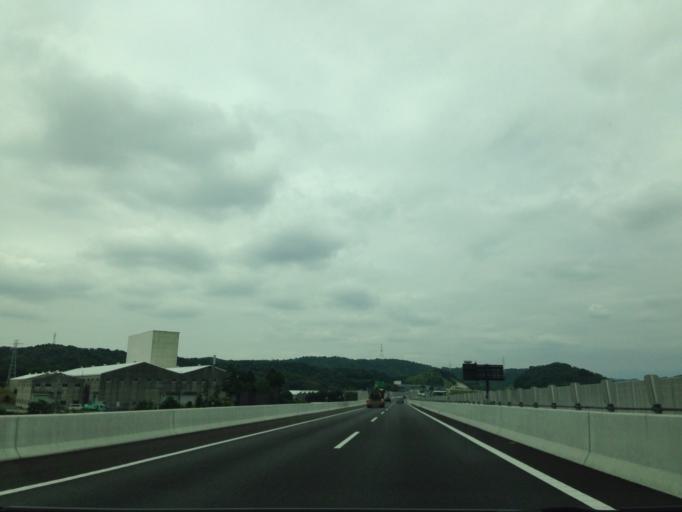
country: JP
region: Aichi
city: Gamagori
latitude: 34.9124
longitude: 137.2886
